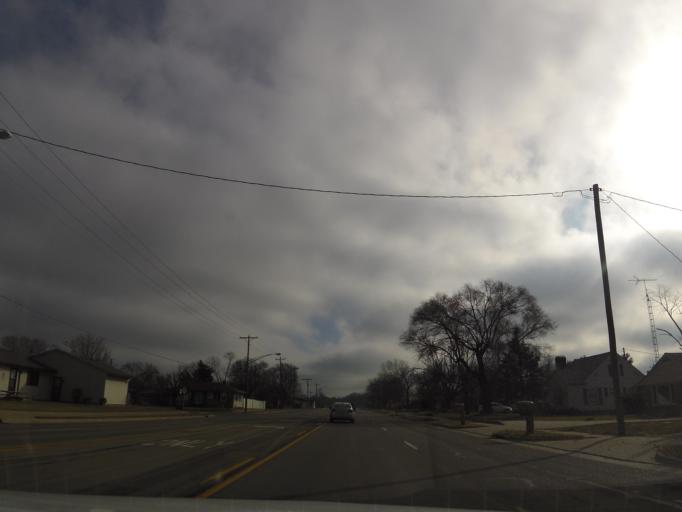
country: US
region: Indiana
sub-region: Bartholomew County
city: Columbus
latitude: 39.1926
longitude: -85.8929
